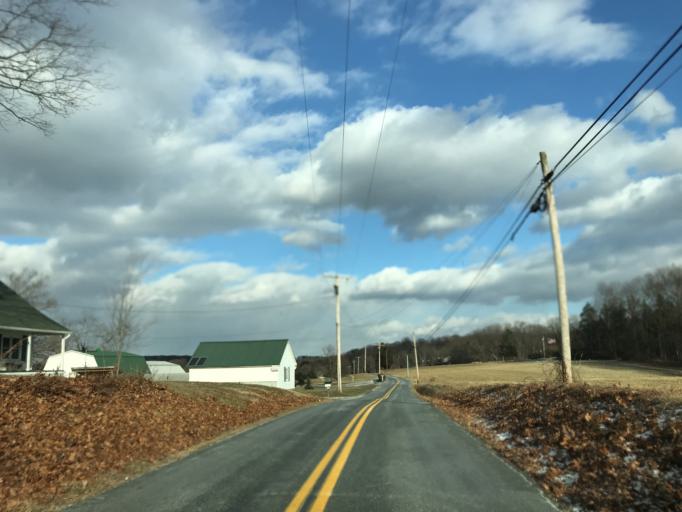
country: US
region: Maryland
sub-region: Harford County
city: Jarrettsville
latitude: 39.6164
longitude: -76.4378
